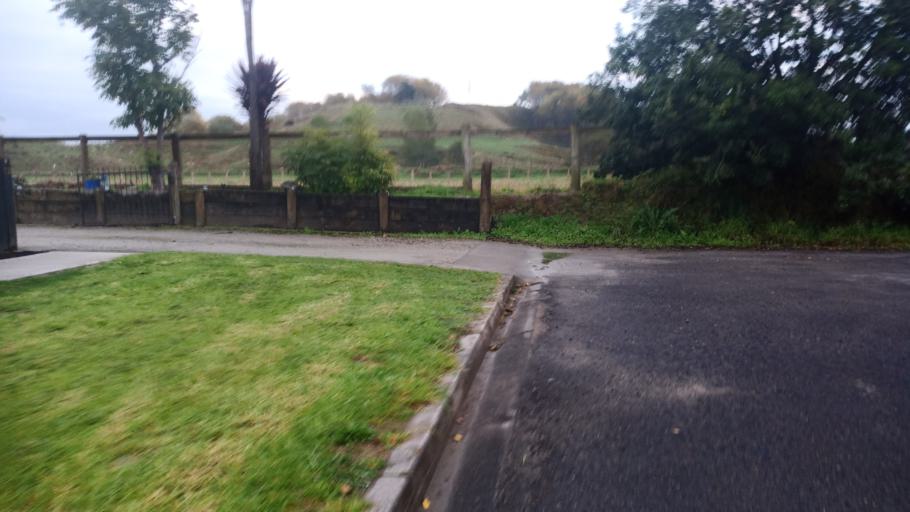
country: NZ
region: Gisborne
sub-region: Gisborne District
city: Gisborne
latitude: -38.6360
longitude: 178.0104
